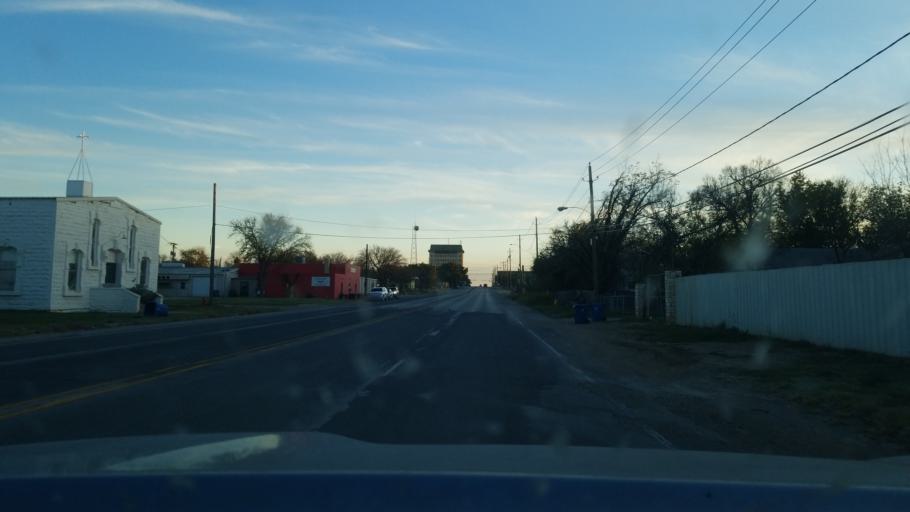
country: US
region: Texas
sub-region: Stephens County
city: Breckenridge
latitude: 32.7611
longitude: -98.9027
